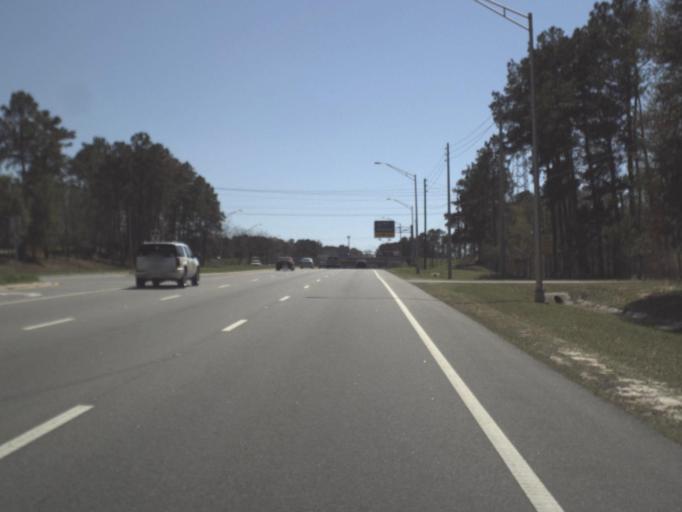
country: US
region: Florida
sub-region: Gadsden County
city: Midway
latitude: 30.4837
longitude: -84.3633
